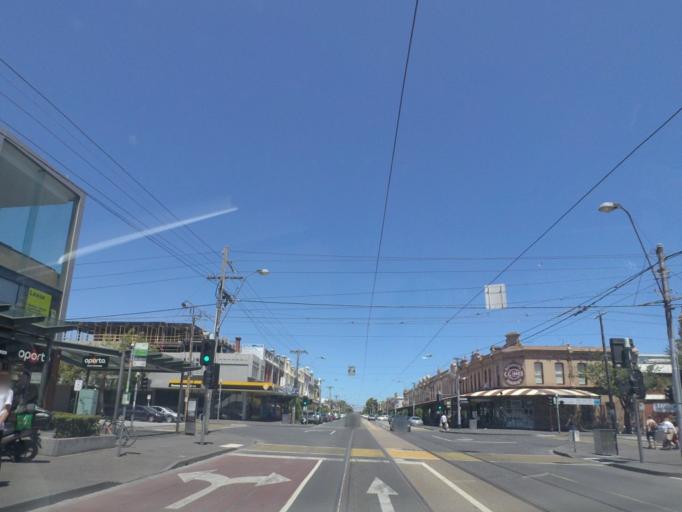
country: AU
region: Victoria
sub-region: Port Phillip
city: South Melbourne
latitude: -37.8325
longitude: 144.9603
